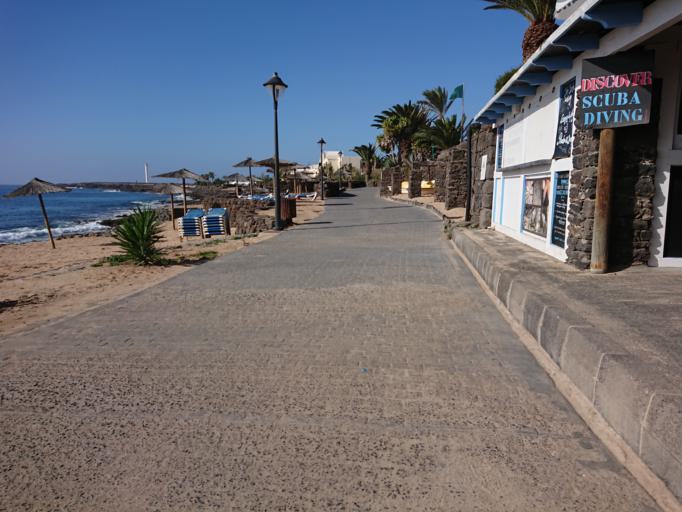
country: ES
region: Canary Islands
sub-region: Provincia de Las Palmas
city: Playa Blanca
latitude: 28.8616
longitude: -13.8605
